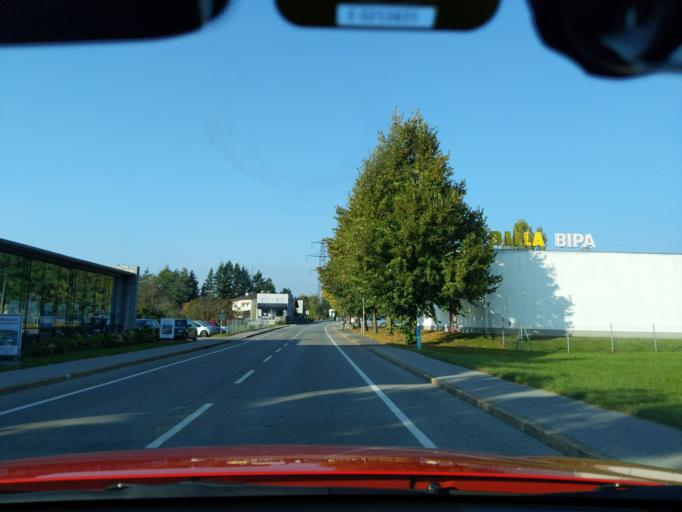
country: AT
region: Vorarlberg
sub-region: Politischer Bezirk Bregenz
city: Lochau
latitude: 47.5357
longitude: 9.7523
